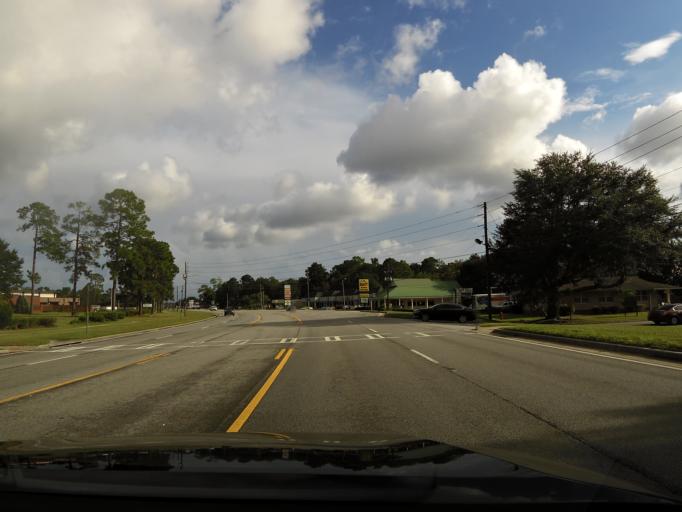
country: US
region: Georgia
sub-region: Liberty County
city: Hinesville
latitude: 31.8492
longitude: -81.6058
